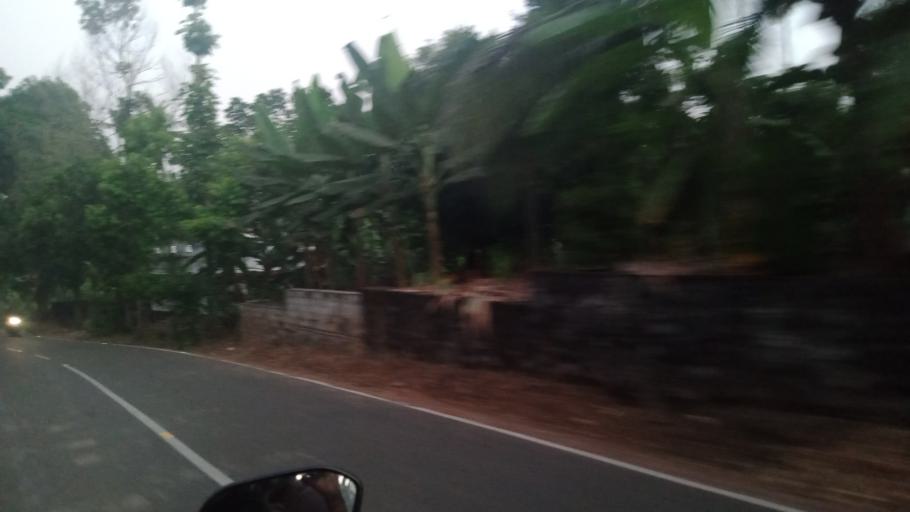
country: IN
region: Kerala
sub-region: Ernakulam
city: Angamali
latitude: 10.2000
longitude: 76.3061
